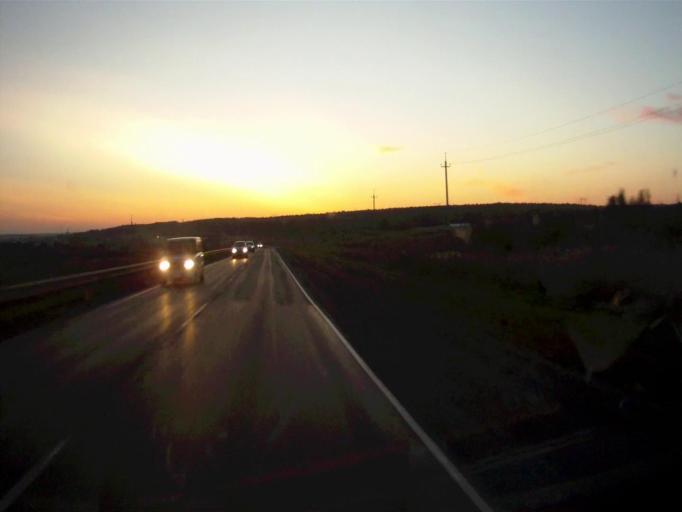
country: RU
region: Chelyabinsk
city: Poletayevo
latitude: 55.2238
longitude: 61.0056
